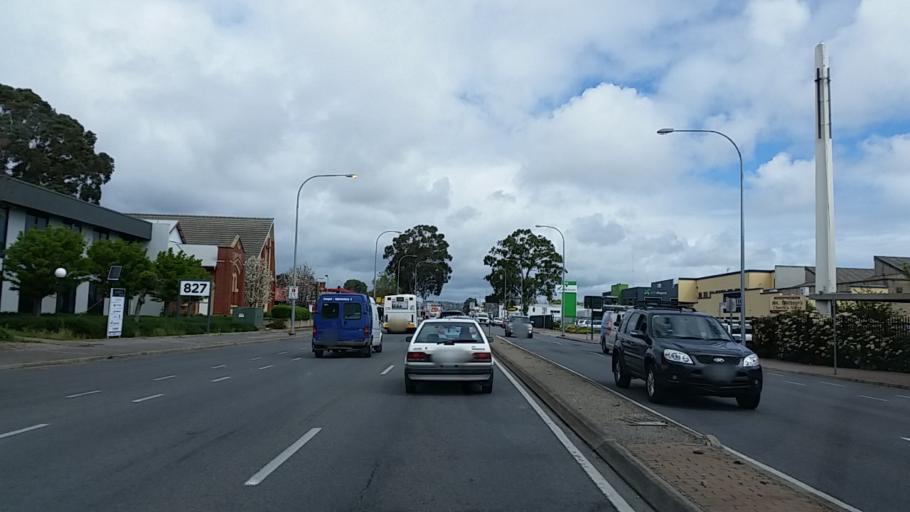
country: AU
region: South Australia
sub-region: Mitcham
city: Clarence Gardens
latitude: -34.9695
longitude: 138.5731
